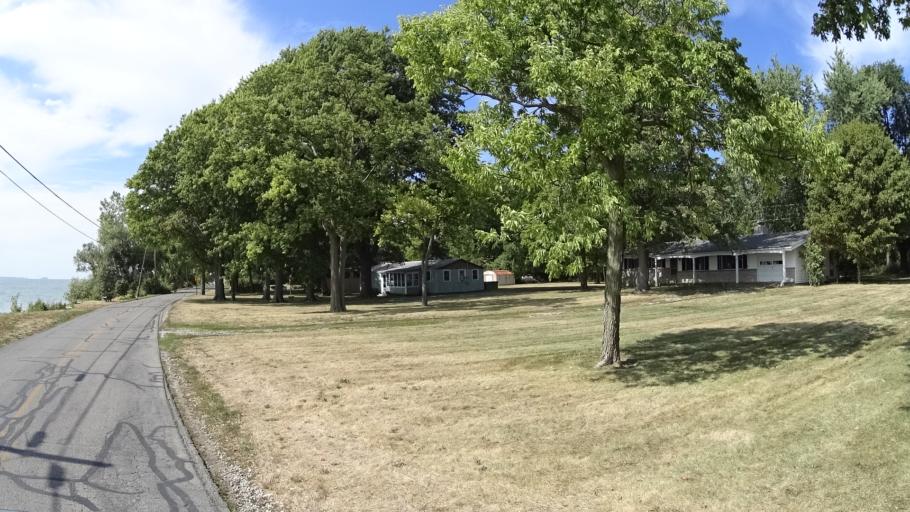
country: US
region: Ohio
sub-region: Erie County
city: Sandusky
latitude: 41.5855
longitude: -82.6989
